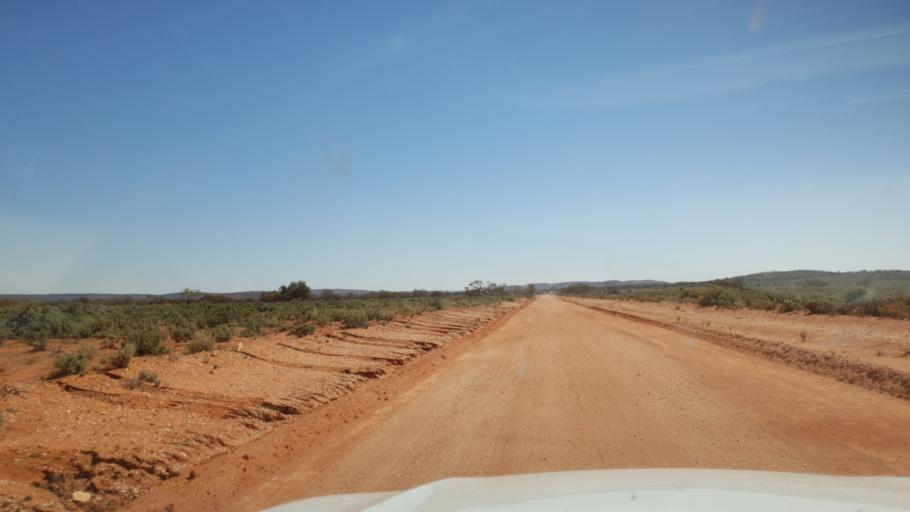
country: AU
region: South Australia
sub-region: Whyalla
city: Whyalla
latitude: -32.6243
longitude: 136.8079
